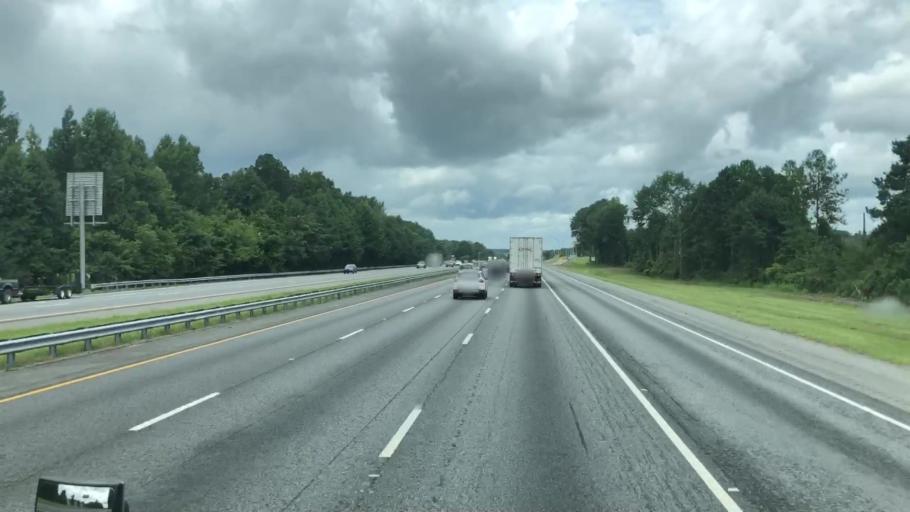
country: US
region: Georgia
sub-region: Monroe County
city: Forsyth
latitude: 33.0651
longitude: -83.9668
